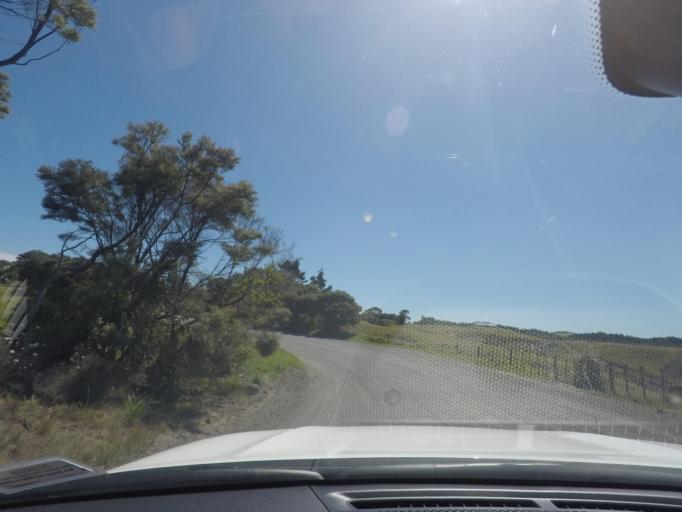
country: NZ
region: Auckland
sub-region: Auckland
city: Parakai
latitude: -36.5820
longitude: 174.3098
